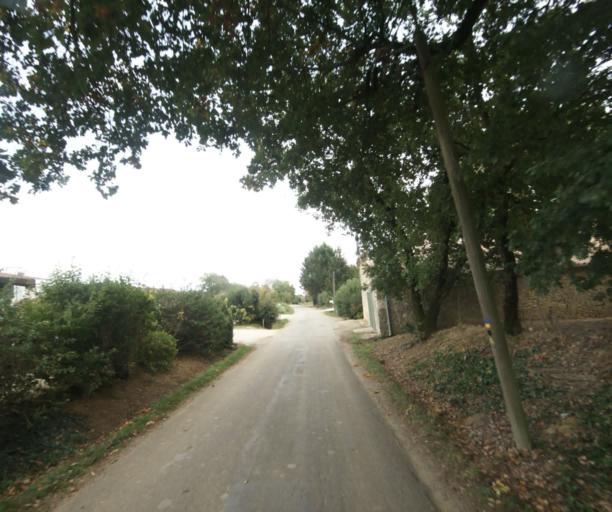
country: FR
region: Midi-Pyrenees
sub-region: Departement du Gers
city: Gondrin
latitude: 43.8730
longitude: 0.2452
